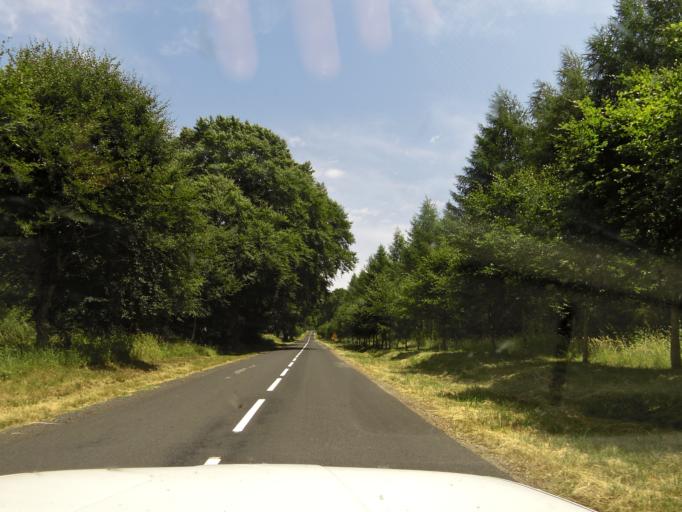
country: FR
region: Auvergne
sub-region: Departement du Puy-de-Dome
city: Orcines
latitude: 45.7638
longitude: 2.9350
